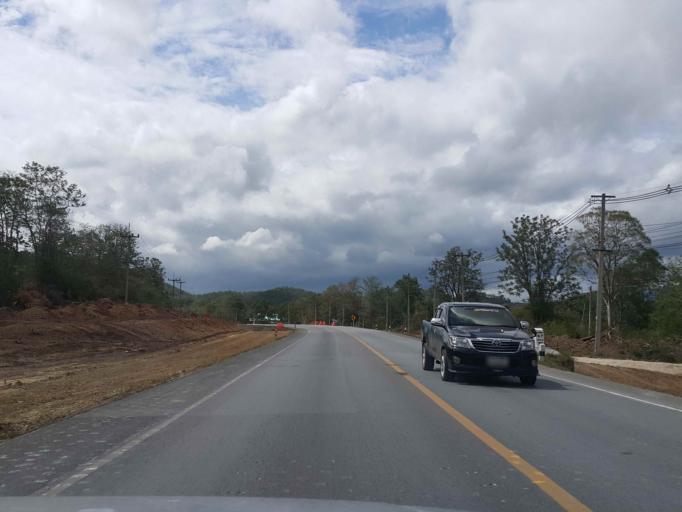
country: TH
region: Tak
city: Tak
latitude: 16.7958
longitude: 99.0101
